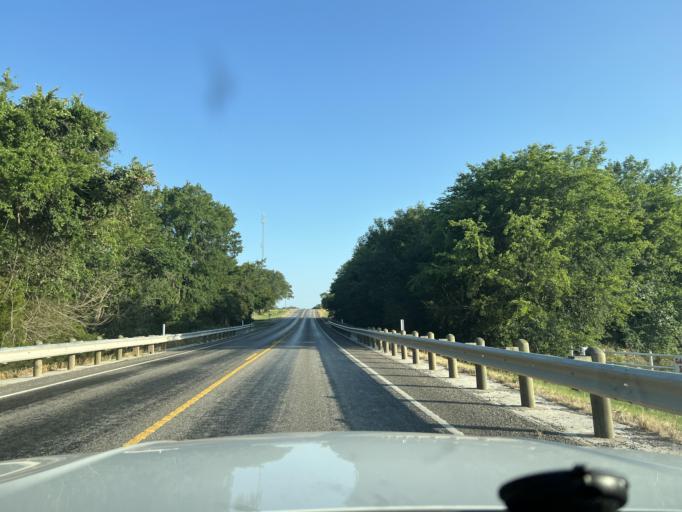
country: US
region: Texas
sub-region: Washington County
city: Brenham
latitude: 30.2115
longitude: -96.3637
